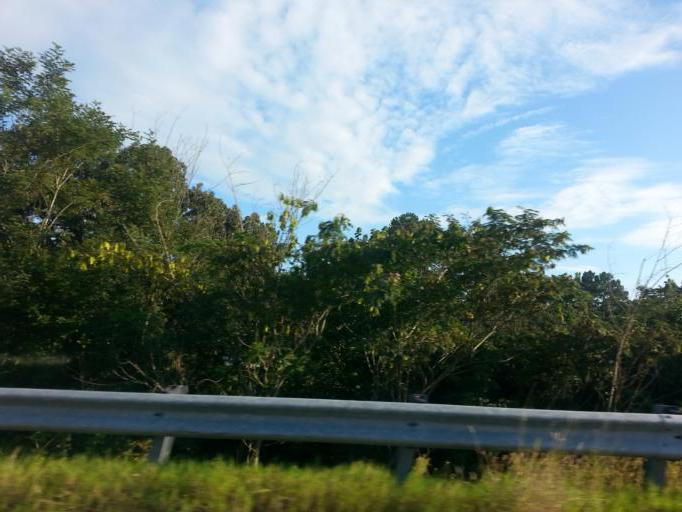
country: US
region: Alabama
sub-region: Lauderdale County
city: Killen
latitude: 34.8595
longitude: -87.4220
